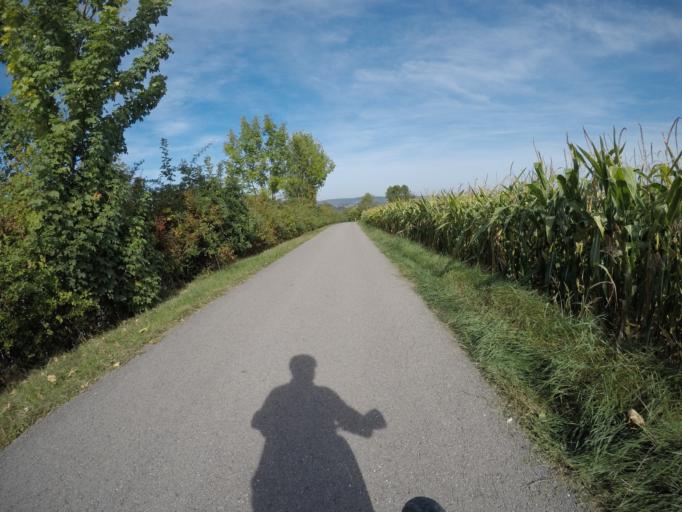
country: DE
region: Baden-Wuerttemberg
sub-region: Regierungsbezirk Stuttgart
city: Markgroningen
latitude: 48.9250
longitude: 9.0688
